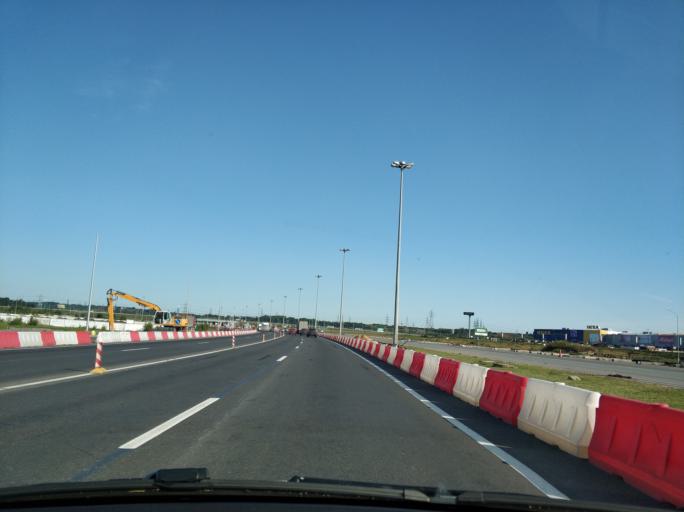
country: RU
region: Leningrad
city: Bugry
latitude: 60.0863
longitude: 30.3766
